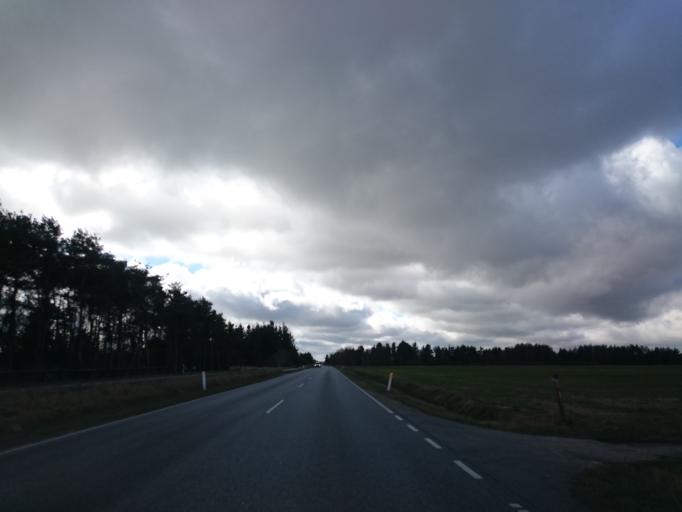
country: DK
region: North Denmark
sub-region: Frederikshavn Kommune
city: Strandby
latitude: 57.6230
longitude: 10.4413
